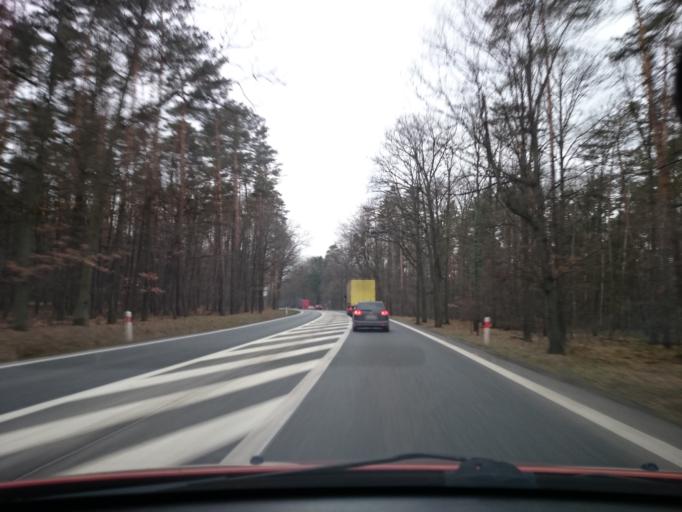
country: PL
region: Opole Voivodeship
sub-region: Powiat opolski
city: Dabrowa
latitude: 50.6866
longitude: 17.7296
